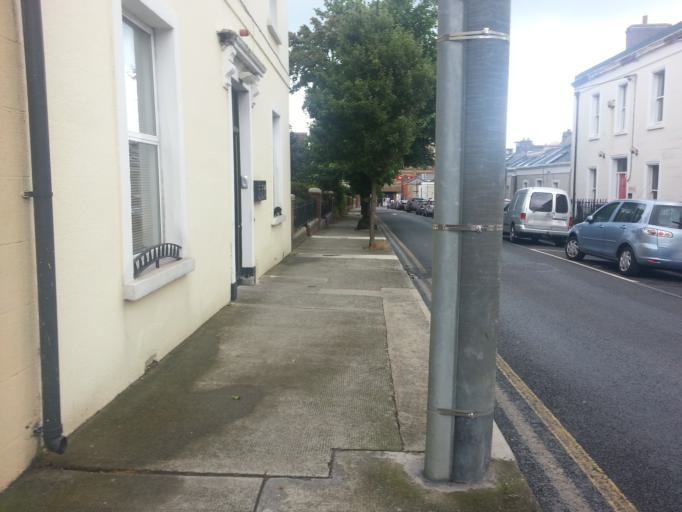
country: IE
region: Leinster
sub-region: Dun Laoghaire-Rathdown
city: Dun Laoghaire
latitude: 53.2909
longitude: -6.1368
